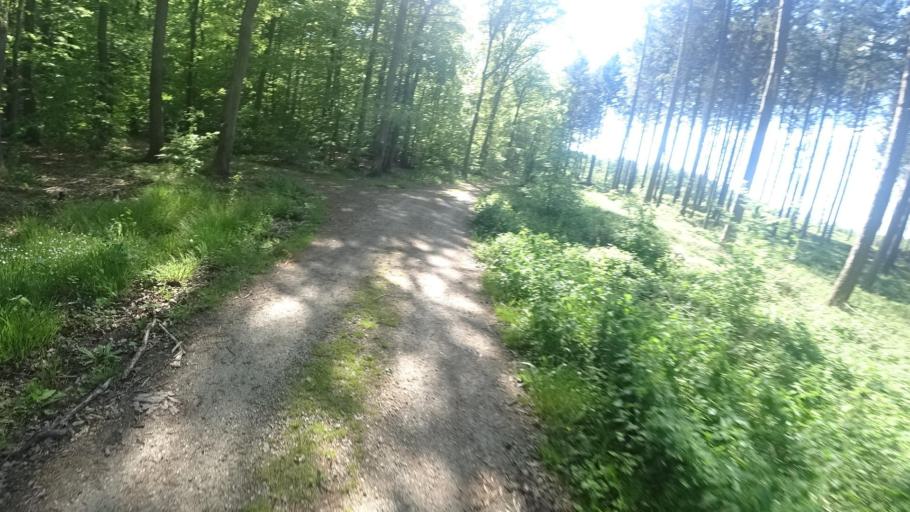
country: DE
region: Rheinland-Pfalz
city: Altenahr
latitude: 50.5182
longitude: 6.9808
